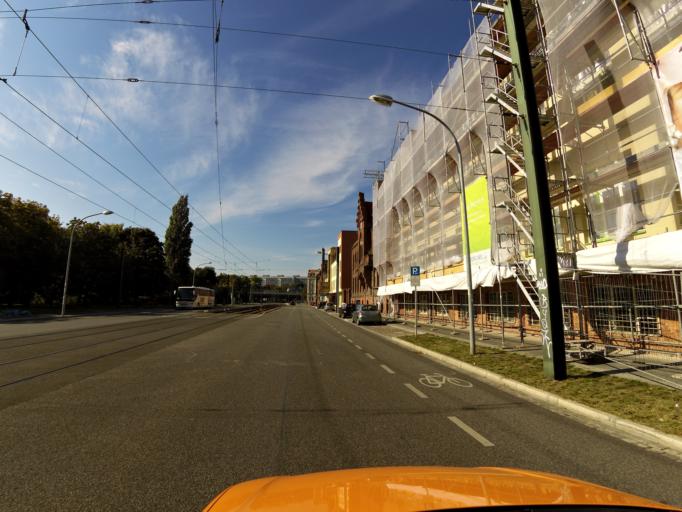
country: DE
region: Brandenburg
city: Potsdam
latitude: 52.3928
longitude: 13.0884
